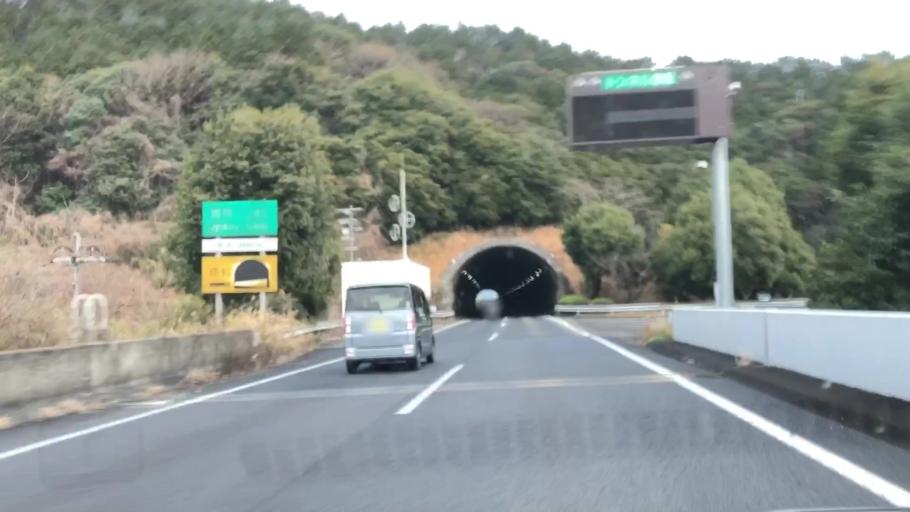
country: JP
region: Saga Prefecture
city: Kanzakimachi-kanzaki
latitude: 33.3401
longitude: 130.3536
